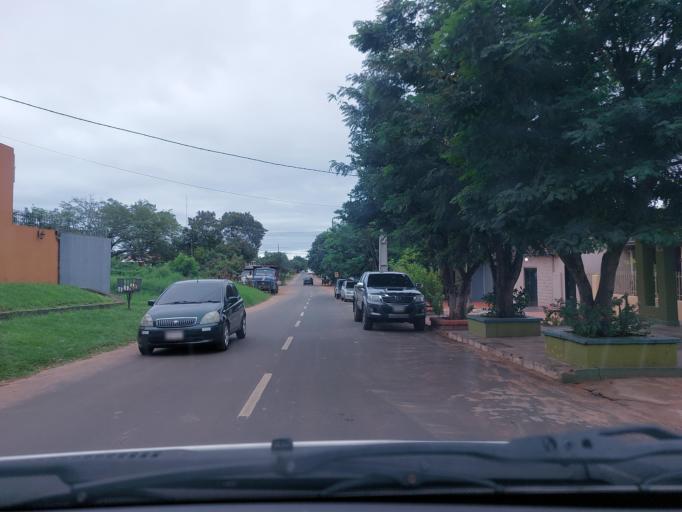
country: PY
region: San Pedro
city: Guayaybi
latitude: -24.6717
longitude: -56.4440
